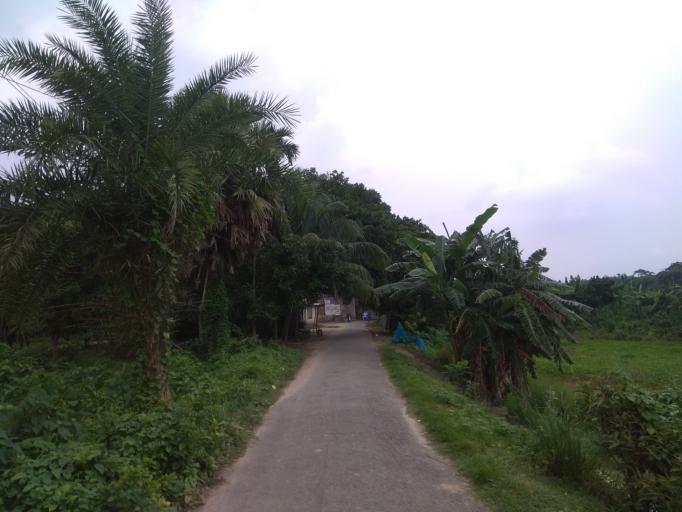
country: BD
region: Dhaka
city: Dohar
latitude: 23.4874
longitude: 90.0298
